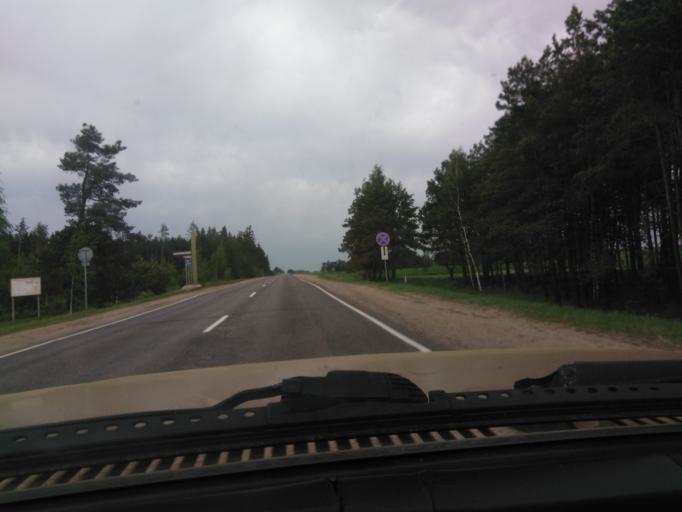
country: BY
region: Mogilev
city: Kamyennyya Lavy
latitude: 54.0442
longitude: 30.3251
